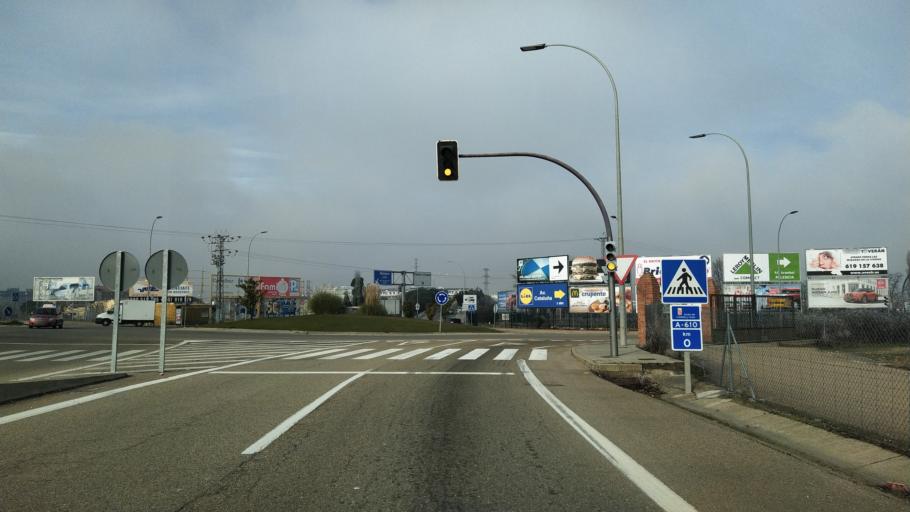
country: ES
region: Castille and Leon
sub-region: Provincia de Palencia
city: Palencia
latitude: 41.9909
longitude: -4.5105
